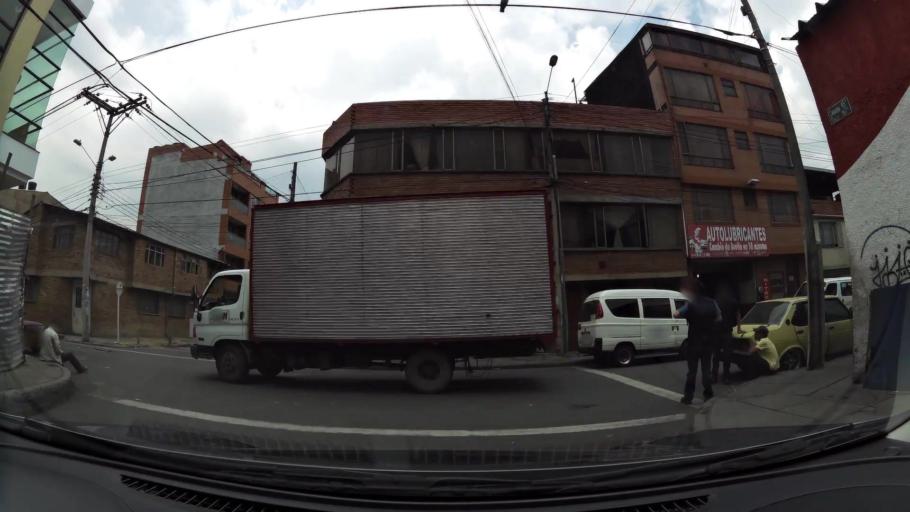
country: CO
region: Cundinamarca
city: Cota
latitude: 4.7487
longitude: -74.0477
